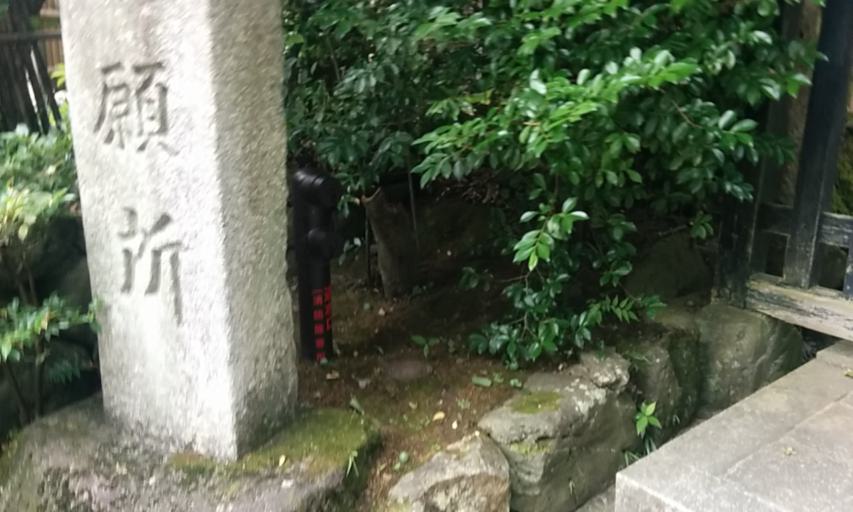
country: JP
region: Kyoto
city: Muko
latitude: 35.0196
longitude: 135.6698
